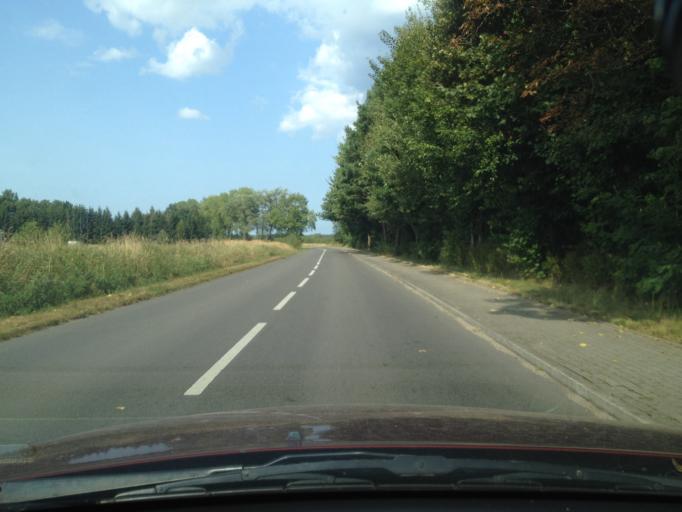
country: PL
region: West Pomeranian Voivodeship
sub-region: Powiat gryficki
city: Pobierowo
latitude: 54.0295
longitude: 14.8740
